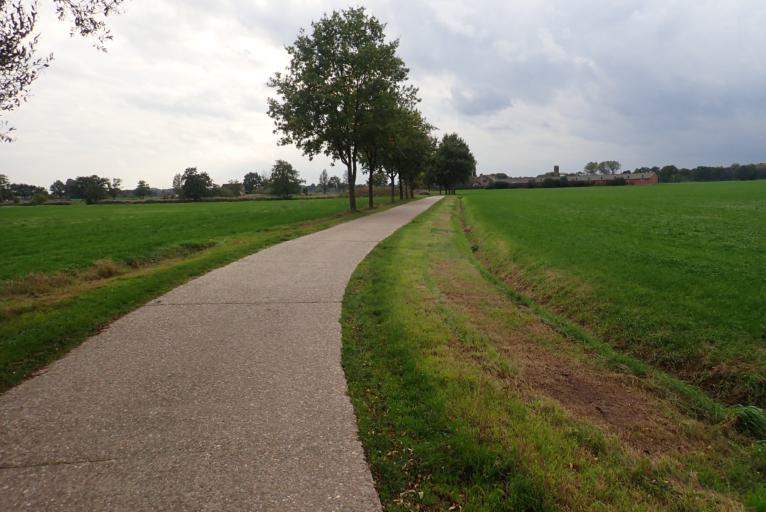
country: BE
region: Flanders
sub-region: Provincie Antwerpen
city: Kalmthout
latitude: 51.4159
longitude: 4.4863
